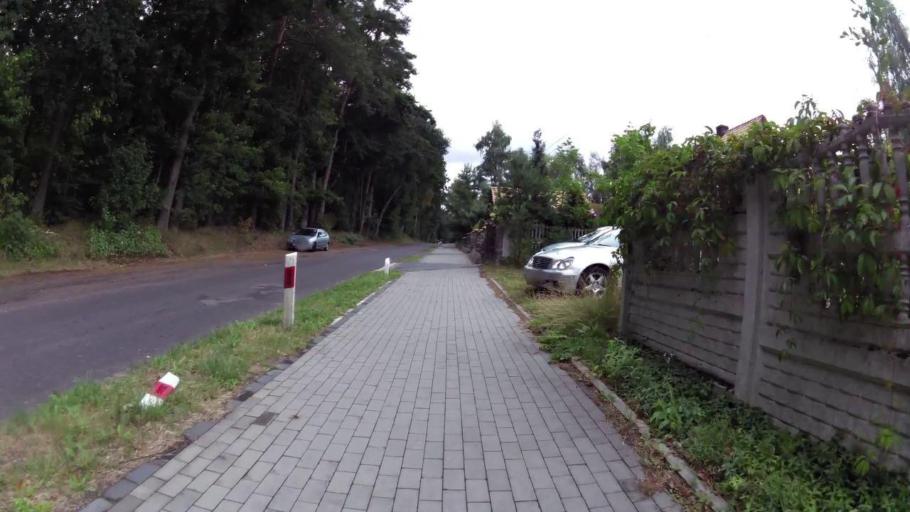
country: PL
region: West Pomeranian Voivodeship
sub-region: Powiat mysliborski
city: Debno
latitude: 52.7589
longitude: 14.6962
